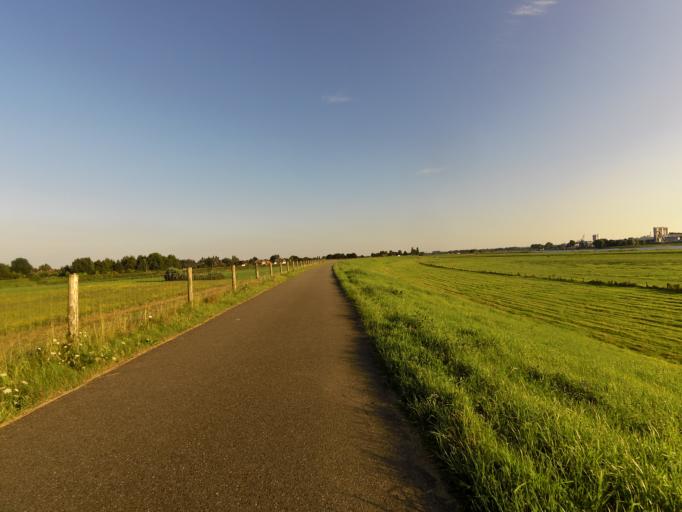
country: NL
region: Gelderland
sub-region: Gemeente Westervoort
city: Westervoort
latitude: 51.9471
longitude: 5.9639
